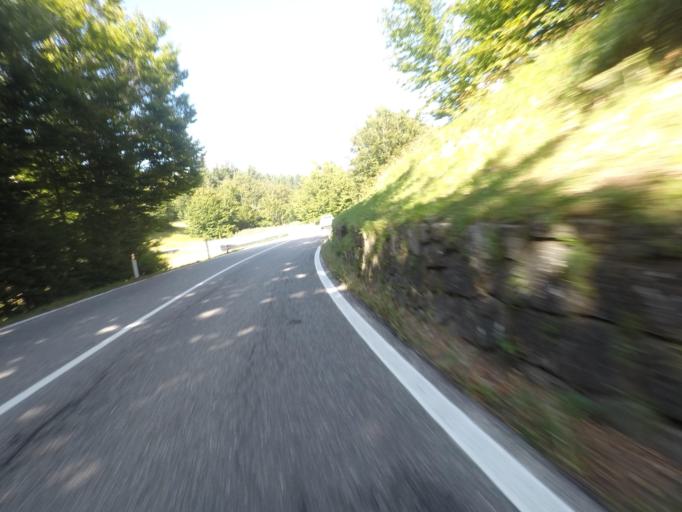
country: IT
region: Emilia-Romagna
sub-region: Provincia di Reggio Emilia
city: Collagna
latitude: 44.2990
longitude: 10.2128
